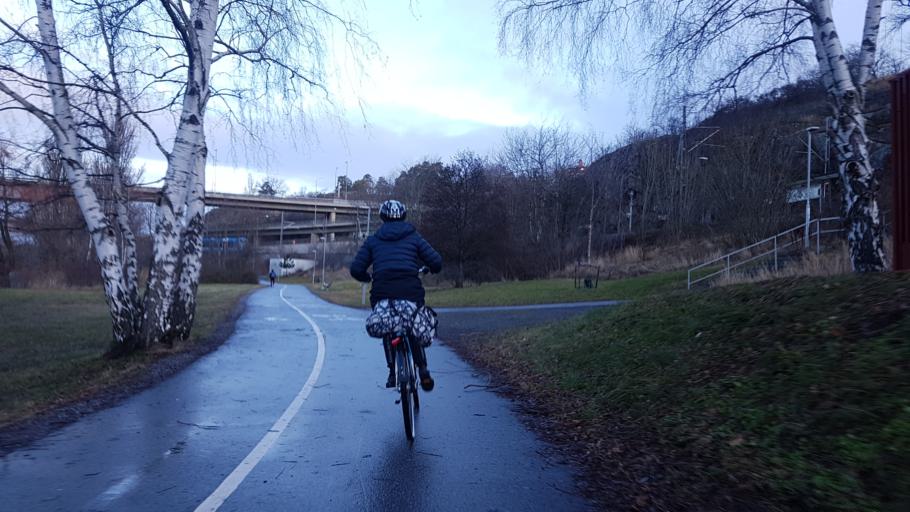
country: SE
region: Stockholm
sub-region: Lidingo
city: Lidingoe
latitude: 59.3612
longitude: 18.1178
